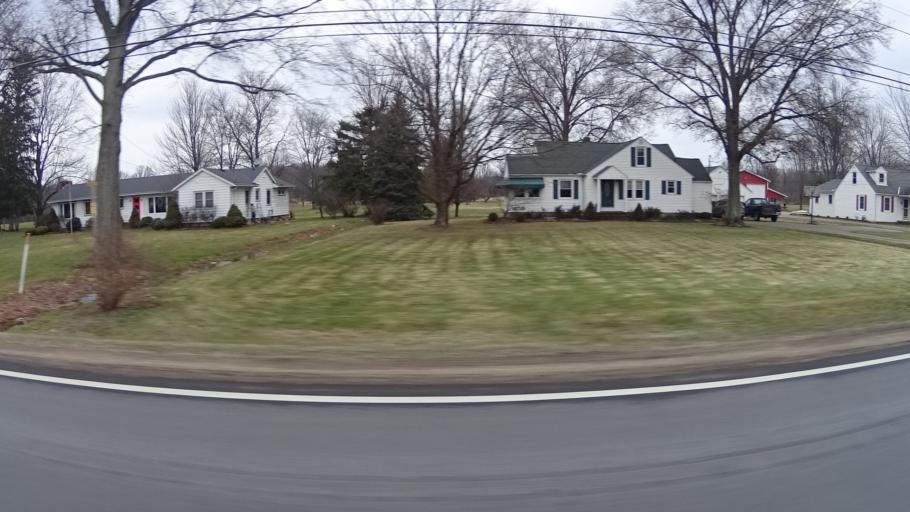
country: US
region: Ohio
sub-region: Lorain County
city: Amherst
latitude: 41.3671
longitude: -82.2009
